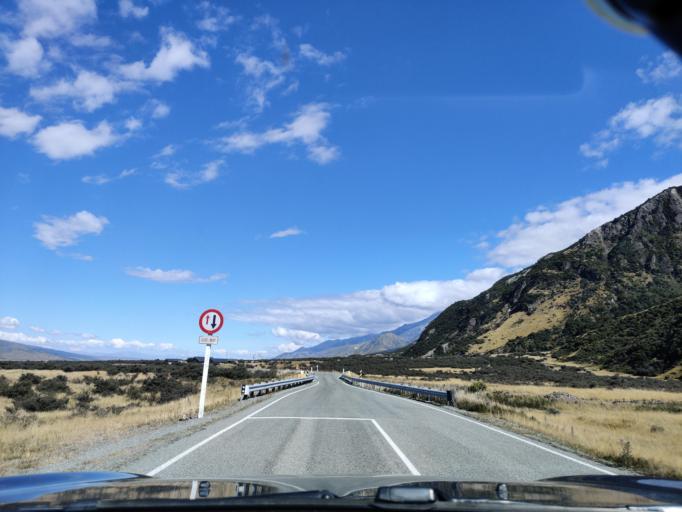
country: NZ
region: Canterbury
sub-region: Timaru District
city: Pleasant Point
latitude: -43.7547
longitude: 170.1175
